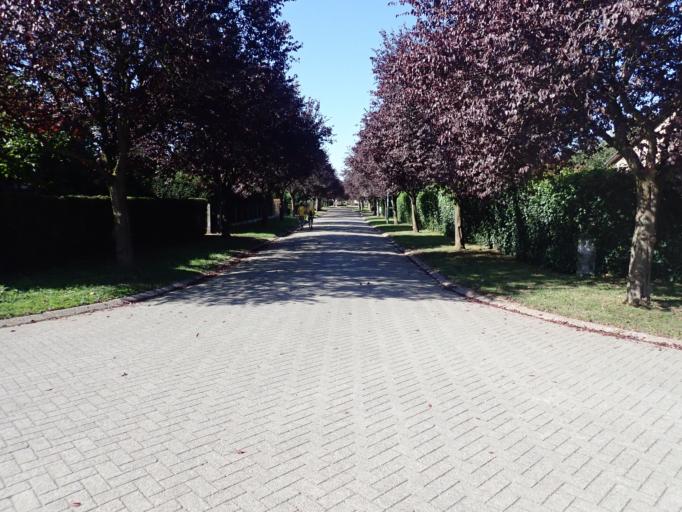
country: BE
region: Flanders
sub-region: Provincie Antwerpen
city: Kasterlee
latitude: 51.2218
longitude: 4.9190
